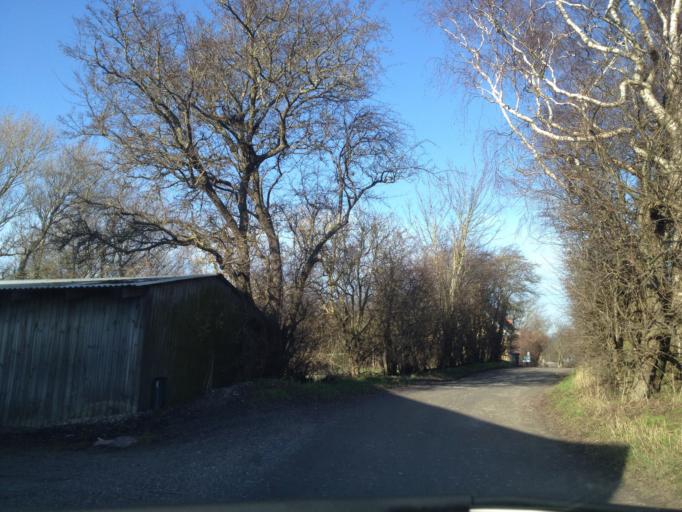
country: DK
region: South Denmark
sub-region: Kerteminde Kommune
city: Munkebo
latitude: 55.5736
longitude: 10.6033
